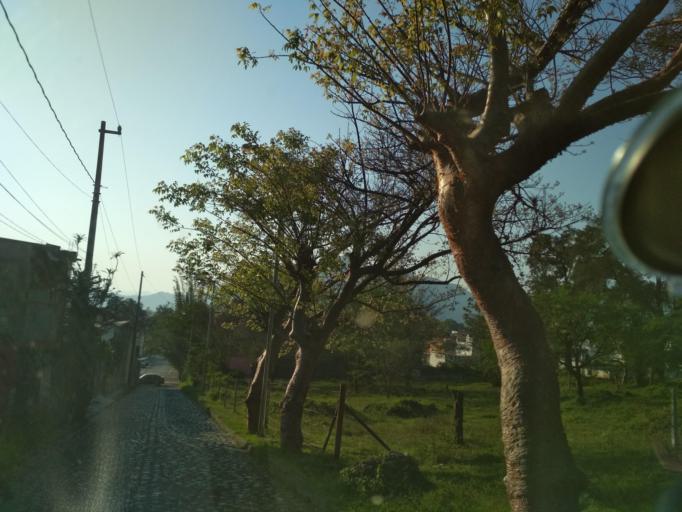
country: MX
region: Veracruz
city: Orizaba
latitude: 18.8606
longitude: -97.0821
